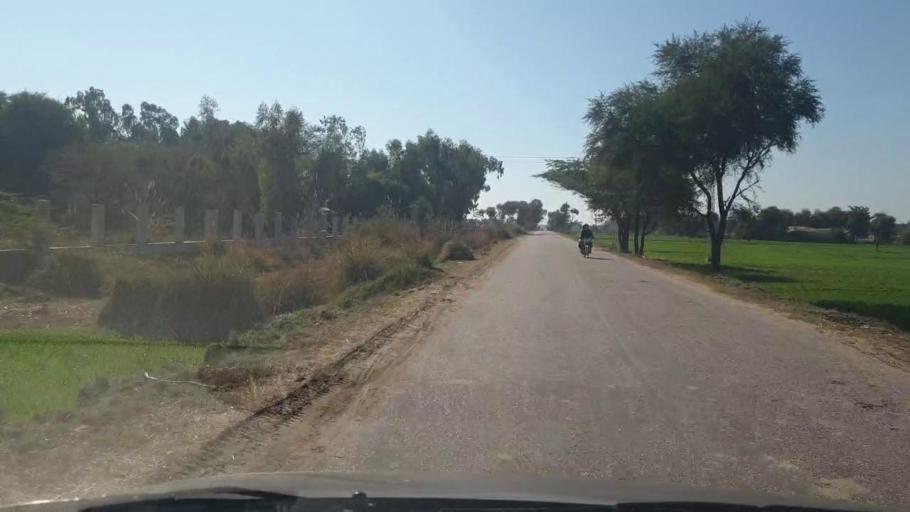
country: PK
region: Sindh
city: Bozdar
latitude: 27.0872
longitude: 68.6233
